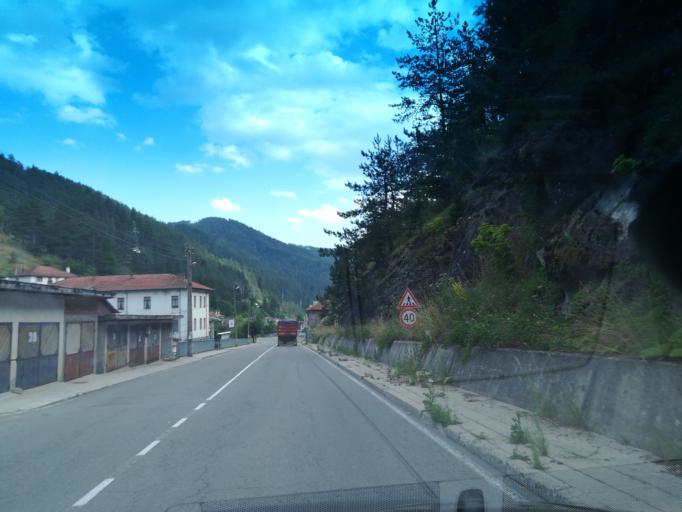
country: BG
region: Smolyan
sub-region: Obshtina Smolyan
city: Smolyan
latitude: 41.6537
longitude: 24.7585
